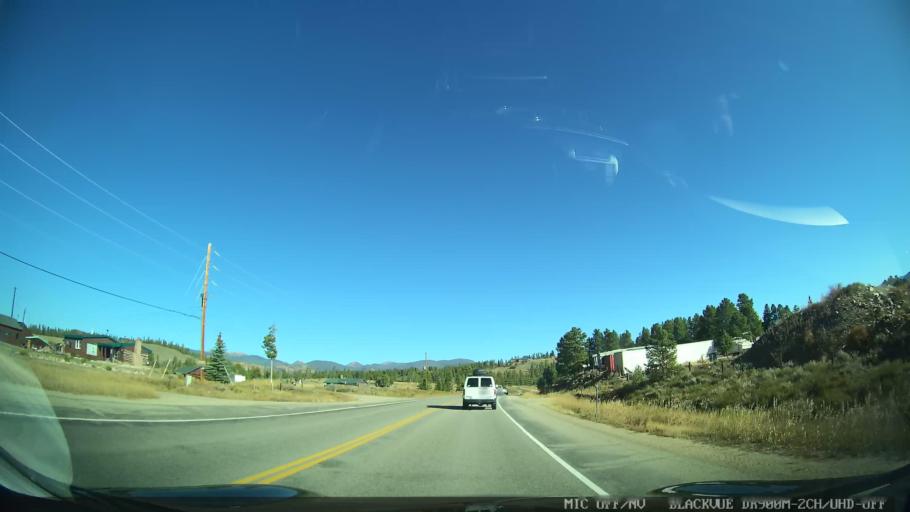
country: US
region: Colorado
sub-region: Grand County
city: Granby
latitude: 40.1714
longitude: -105.9006
